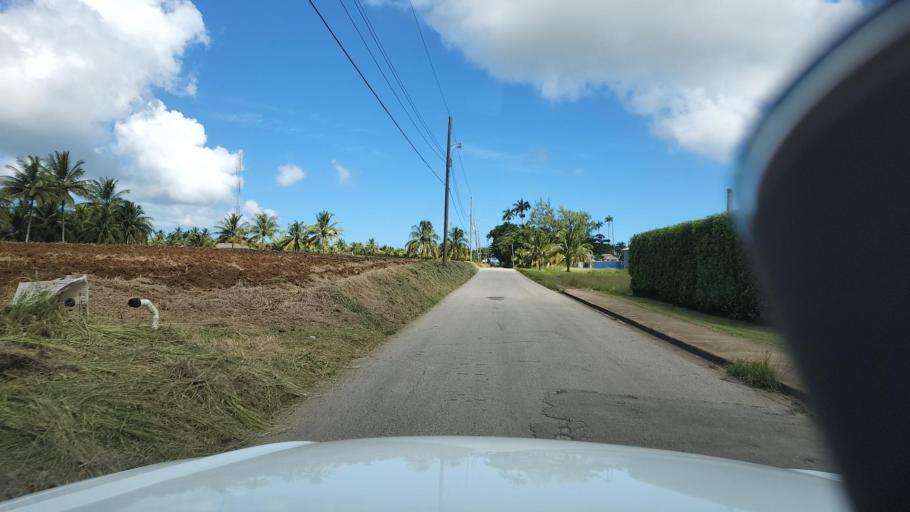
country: BB
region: Saint Thomas
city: Welchman Hall
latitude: 13.1869
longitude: -59.5673
